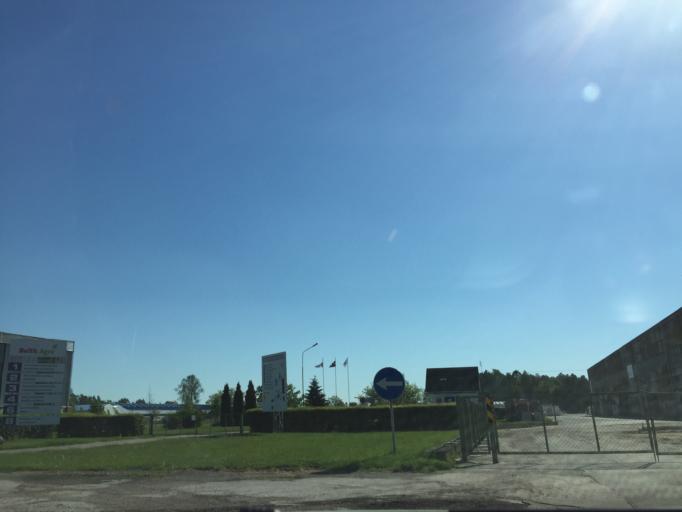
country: LV
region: Ozolnieku
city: Ozolnieki
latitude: 56.6656
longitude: 23.8037
